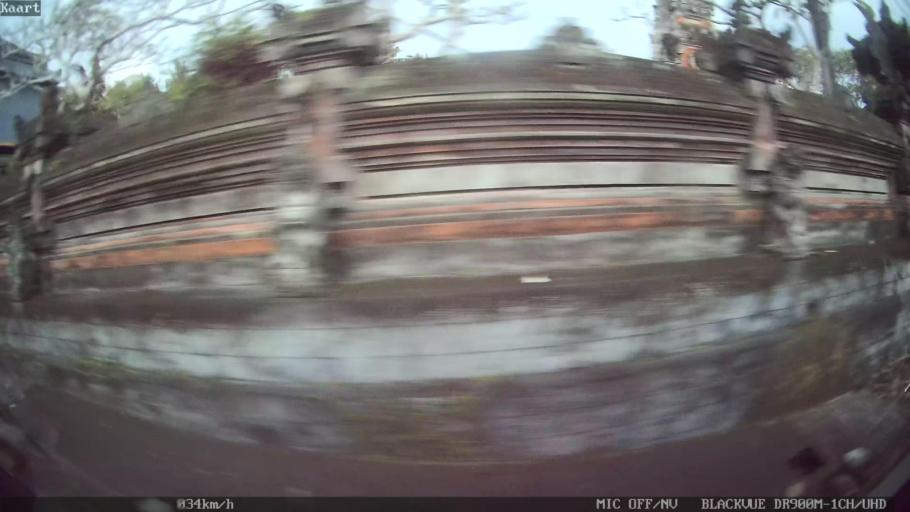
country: ID
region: Bali
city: Banjar Tebongkang
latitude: -8.5267
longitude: 115.2486
